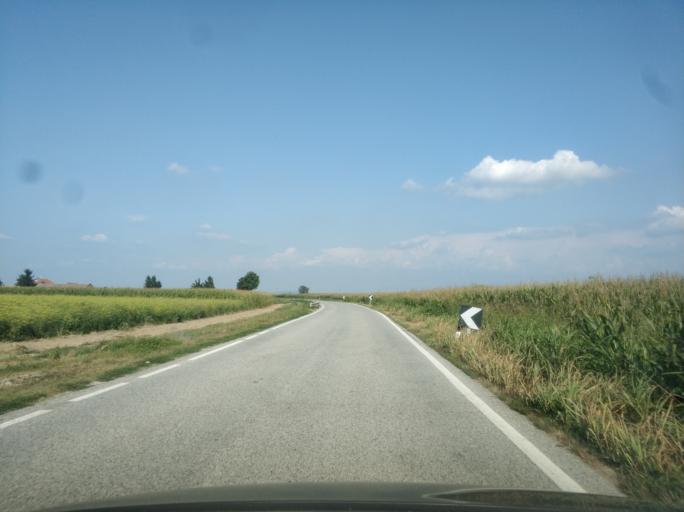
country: IT
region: Piedmont
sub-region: Provincia di Cuneo
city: Genola
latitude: 44.5326
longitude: 7.6493
